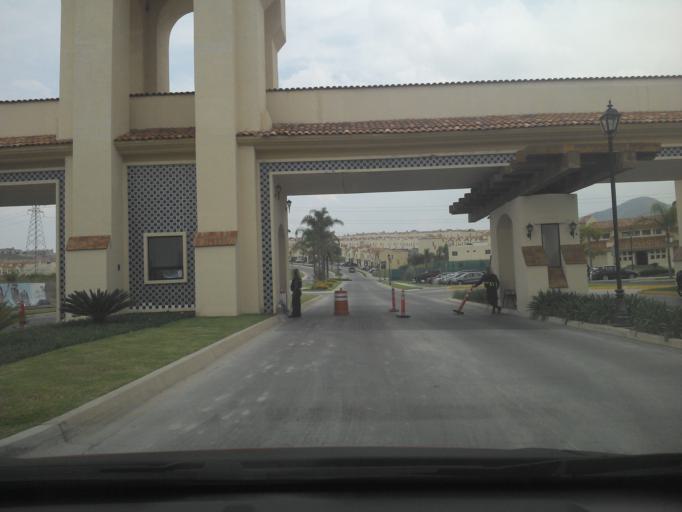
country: MX
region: Jalisco
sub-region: Tlajomulco de Zuniga
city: Lomas de San Agustin
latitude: 20.5292
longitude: -103.4633
